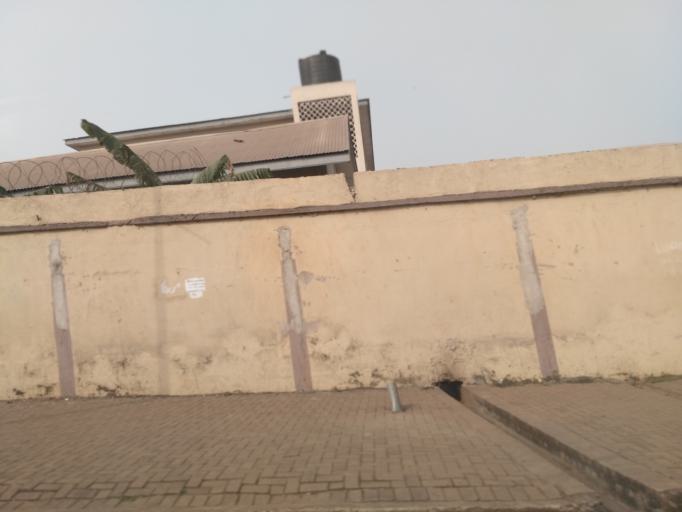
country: GH
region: Ashanti
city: Kumasi
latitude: 6.6929
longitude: -1.6072
